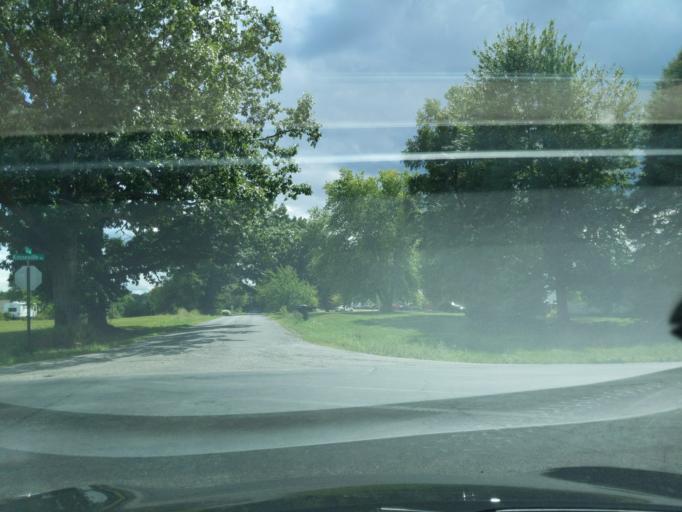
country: US
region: Michigan
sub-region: Eaton County
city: Eaton Rapids
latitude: 42.4657
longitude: -84.5805
